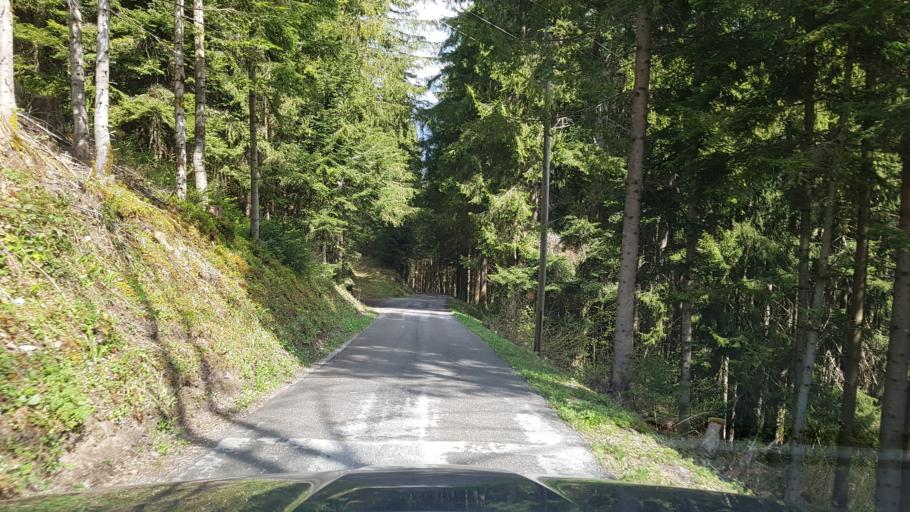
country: AT
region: Salzburg
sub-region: Politischer Bezirk Sankt Johann im Pongau
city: Werfen
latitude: 47.4637
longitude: 13.1802
